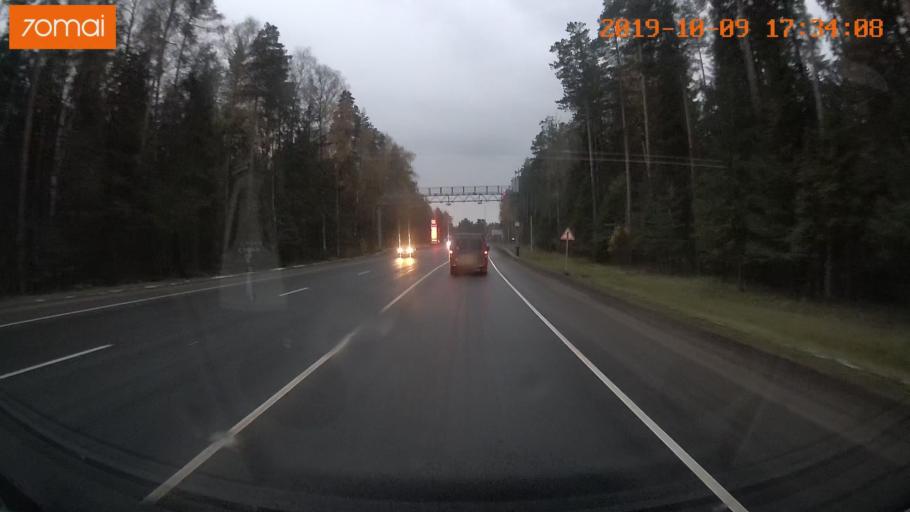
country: RU
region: Ivanovo
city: Bogorodskoye
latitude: 57.1094
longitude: 41.0148
